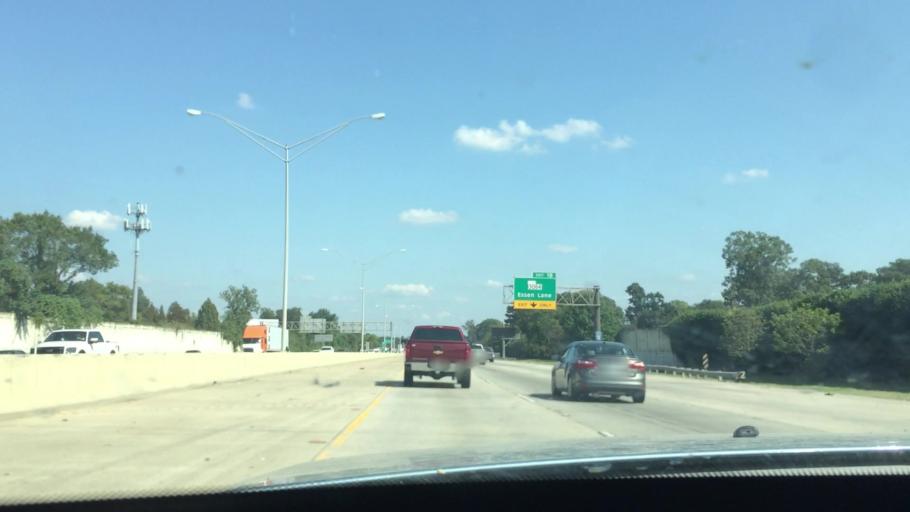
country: US
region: Louisiana
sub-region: East Baton Rouge Parish
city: Westminster
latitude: 30.4180
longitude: -91.1061
